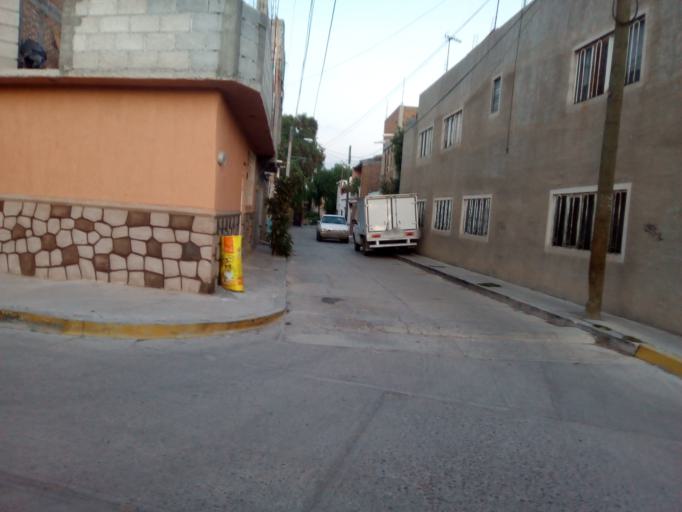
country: MX
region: Guerrero
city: San Luis de la Paz
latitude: 21.2915
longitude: -100.5197
